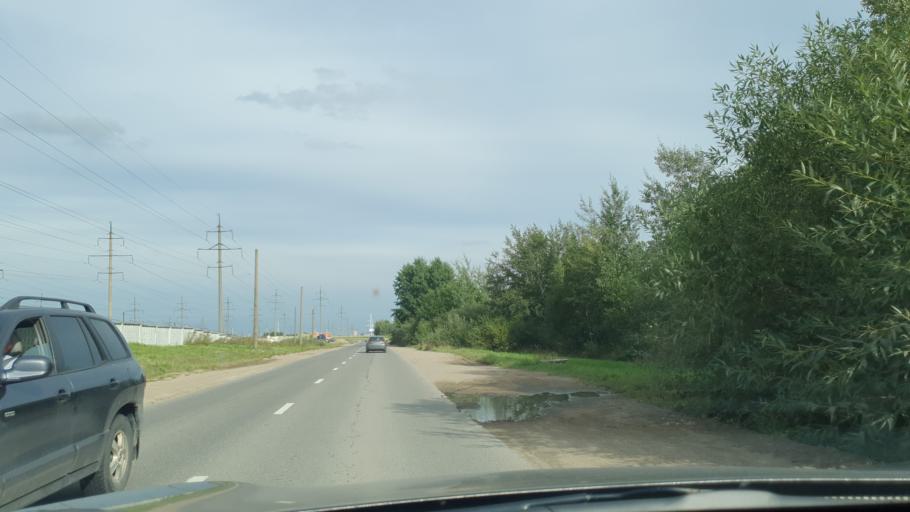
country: BY
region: Minsk
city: Azyartso
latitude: 53.8681
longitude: 27.4048
